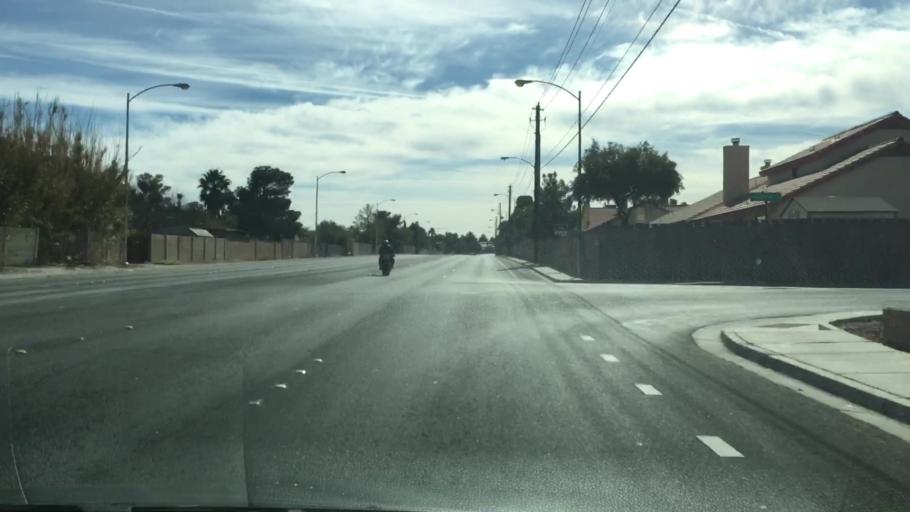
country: US
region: Nevada
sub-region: Clark County
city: Whitney
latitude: 36.0459
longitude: -115.1274
